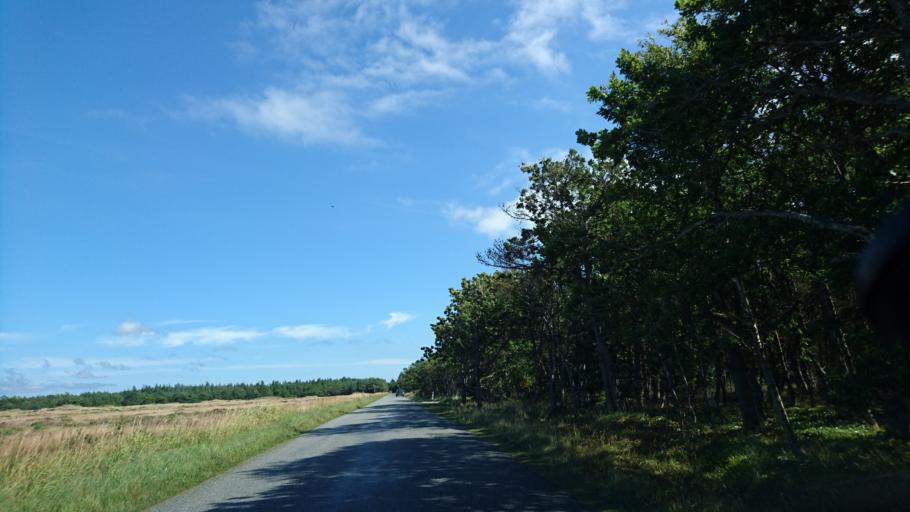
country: DK
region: North Denmark
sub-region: Frederikshavn Kommune
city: Strandby
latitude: 57.6279
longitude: 10.4182
